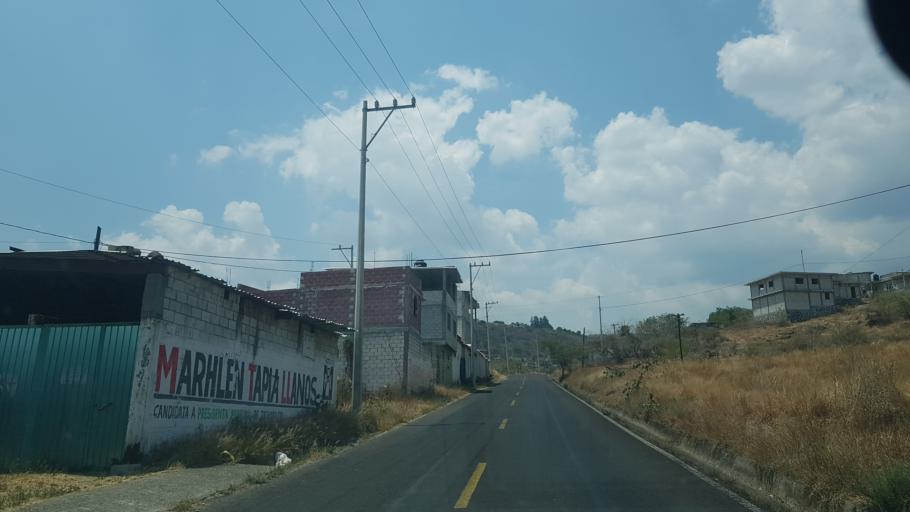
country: MX
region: Puebla
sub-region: Atzitzihuacan
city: Santiago Atzitzihuacan
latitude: 18.8336
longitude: -98.5925
